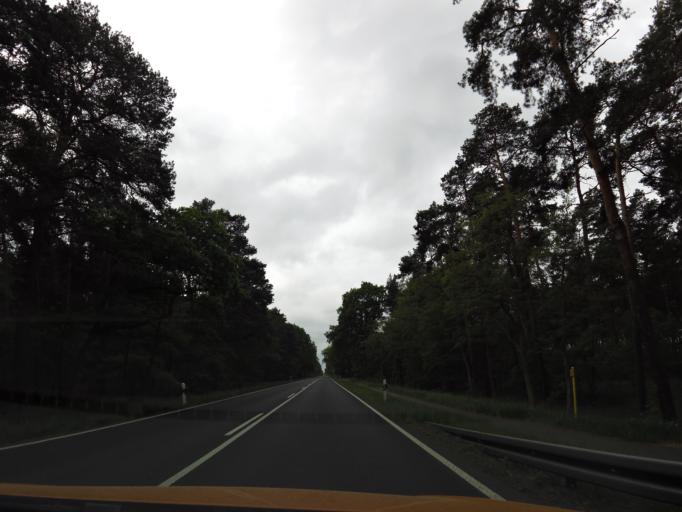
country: DE
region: Brandenburg
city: Treuenbrietzen
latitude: 52.1475
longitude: 12.9217
